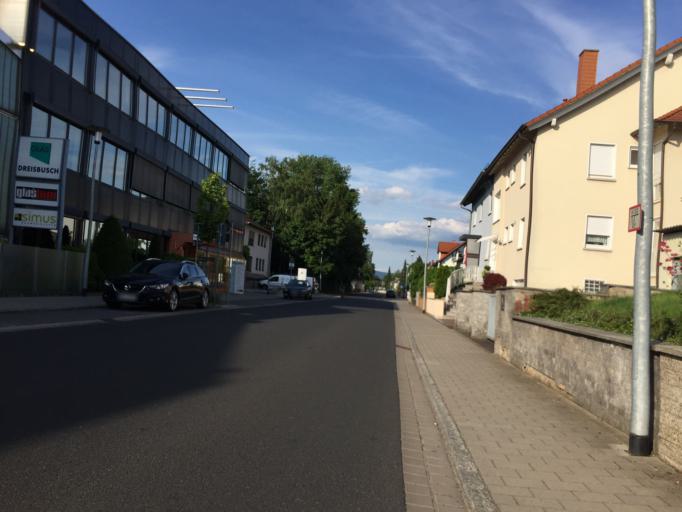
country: DE
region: Bavaria
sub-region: Regierungsbezirk Unterfranken
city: Goldbach
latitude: 49.9888
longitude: 9.1785
